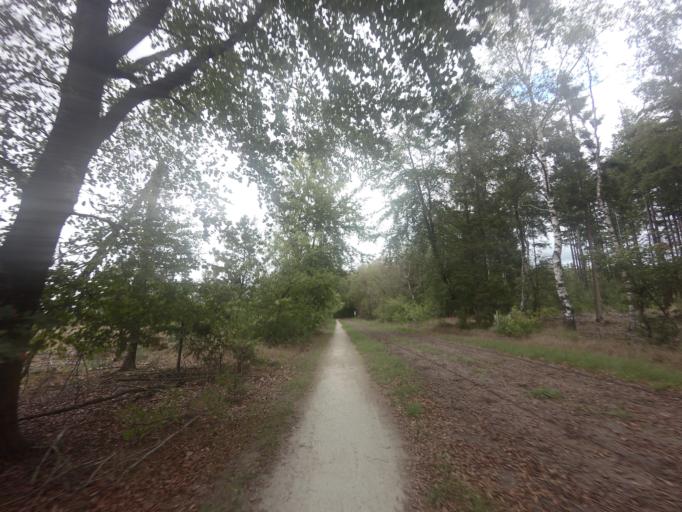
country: NL
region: Drenthe
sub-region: Gemeente Westerveld
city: Dwingeloo
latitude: 52.9263
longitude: 6.3206
